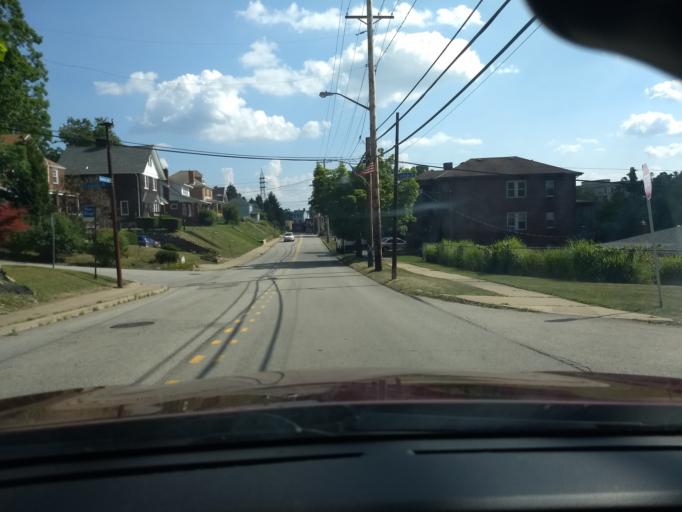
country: US
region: Pennsylvania
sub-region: Allegheny County
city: West Homestead
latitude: 40.3722
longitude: -79.9123
